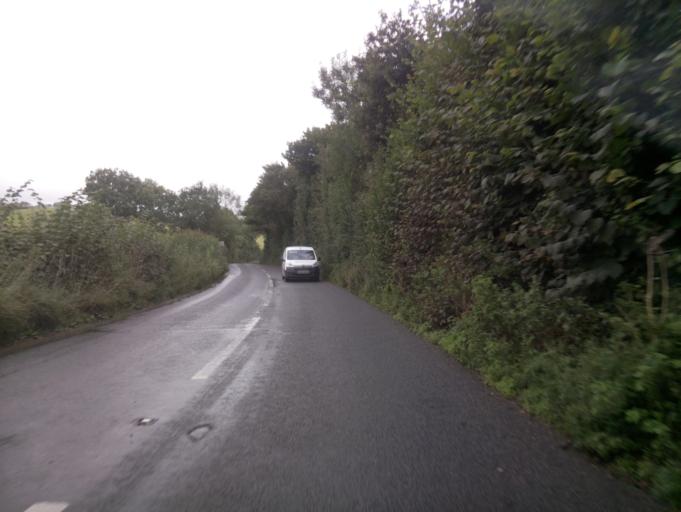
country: GB
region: England
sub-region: Devon
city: Modbury
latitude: 50.3307
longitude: -3.8458
